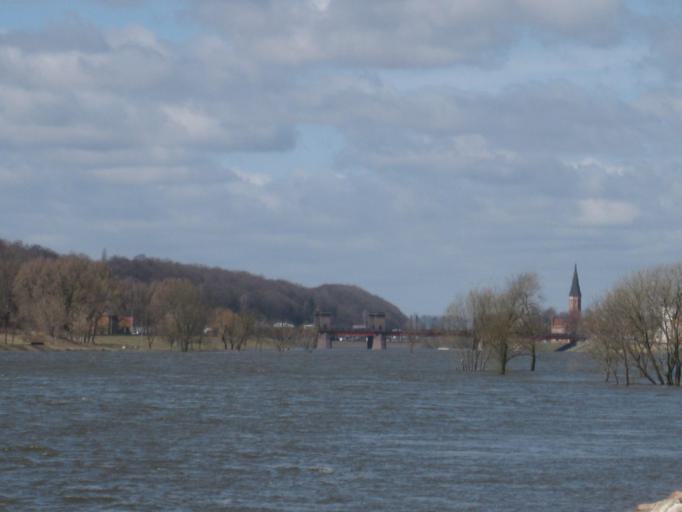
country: LT
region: Kauno apskritis
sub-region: Kaunas
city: Aleksotas
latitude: 54.8903
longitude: 23.9128
